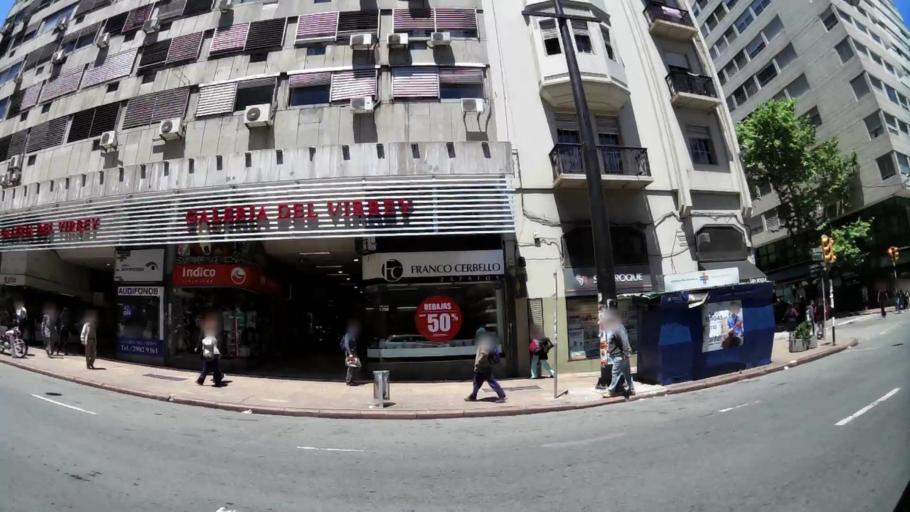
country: UY
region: Montevideo
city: Montevideo
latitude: -34.9058
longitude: -56.1889
